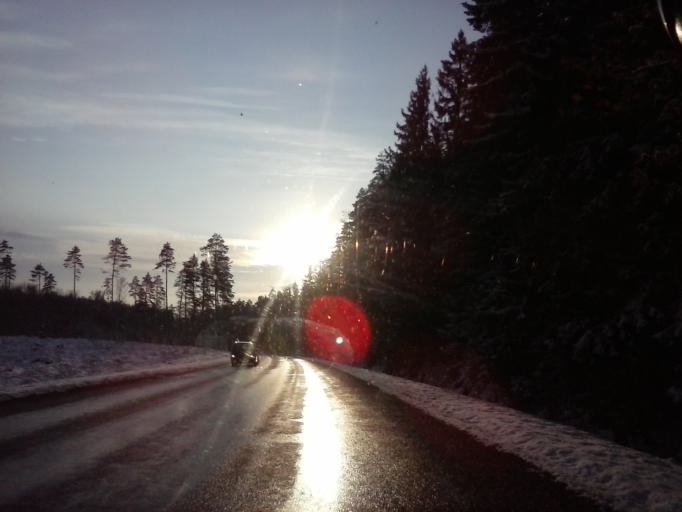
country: EE
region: Tartu
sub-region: UElenurme vald
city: Ulenurme
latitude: 58.3386
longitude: 26.8990
